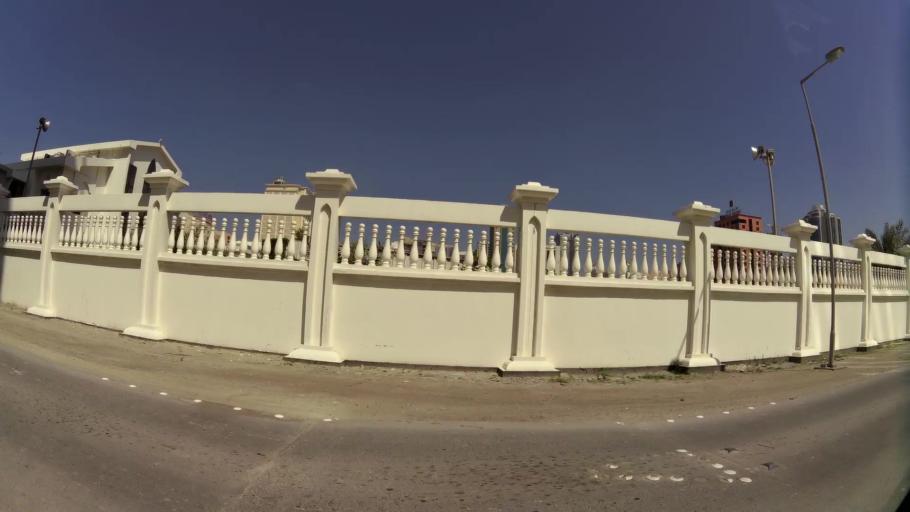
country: BH
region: Manama
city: Manama
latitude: 26.2152
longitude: 50.6061
